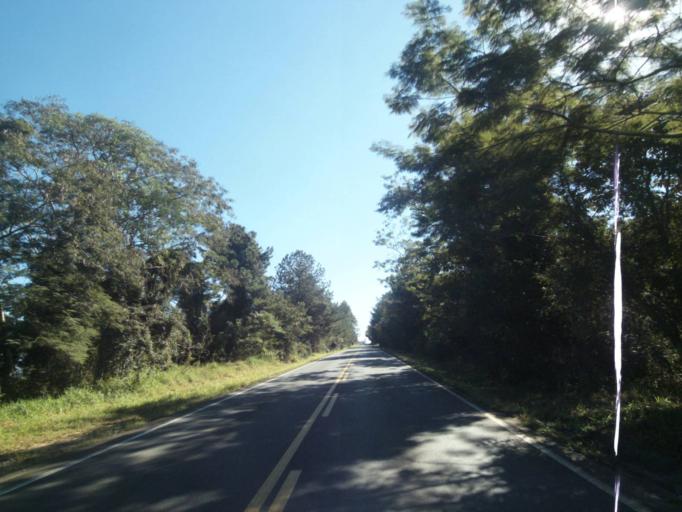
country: BR
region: Parana
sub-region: Tibagi
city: Tibagi
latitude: -24.4686
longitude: -50.5380
